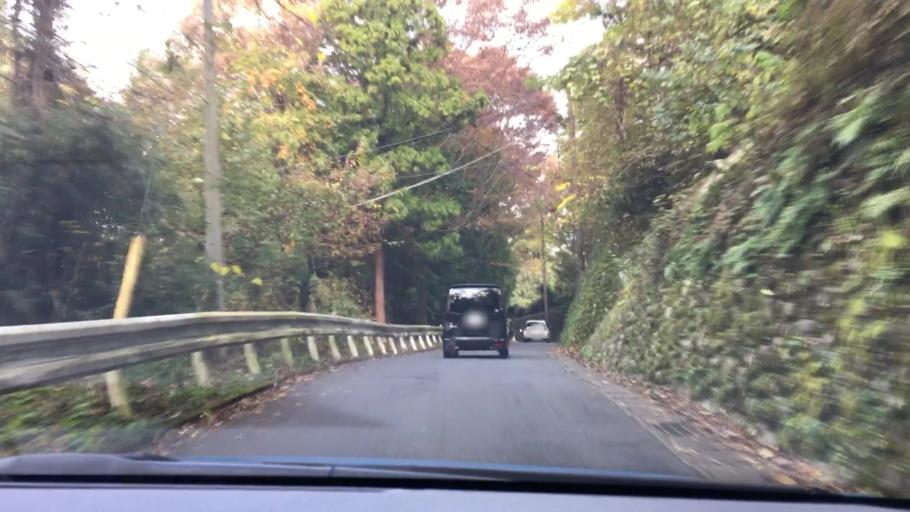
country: JP
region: Yamanashi
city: Uenohara
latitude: 35.5580
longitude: 139.1697
